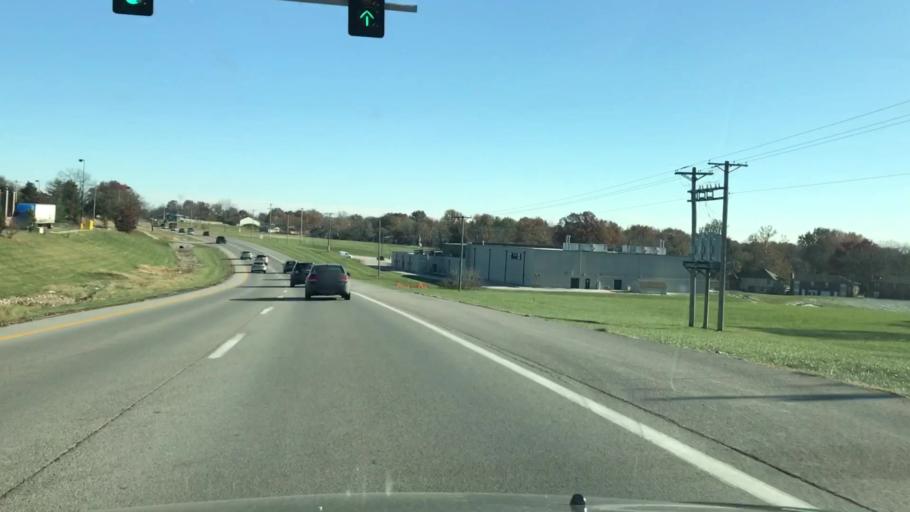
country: US
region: Missouri
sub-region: Jackson County
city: Raytown
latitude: 38.9839
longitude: -94.4621
